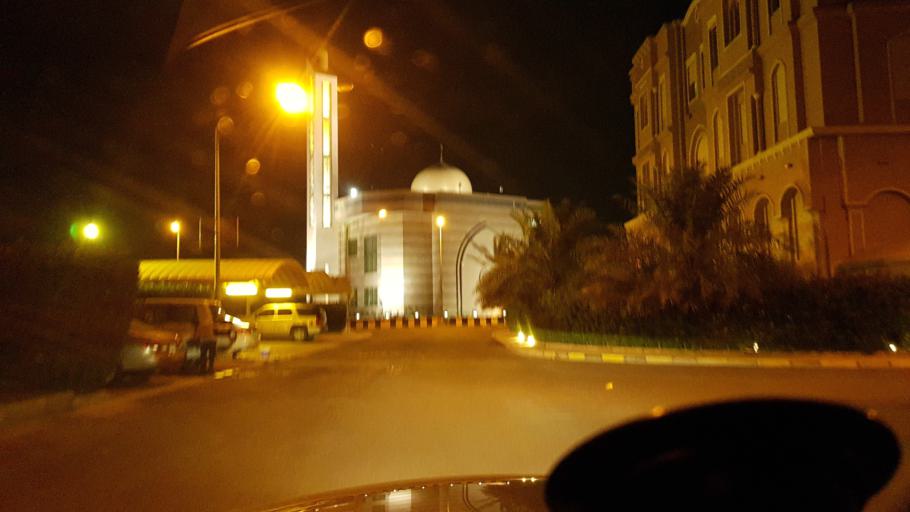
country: KW
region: Al Ahmadi
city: Al Manqaf
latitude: 29.1178
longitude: 48.1282
